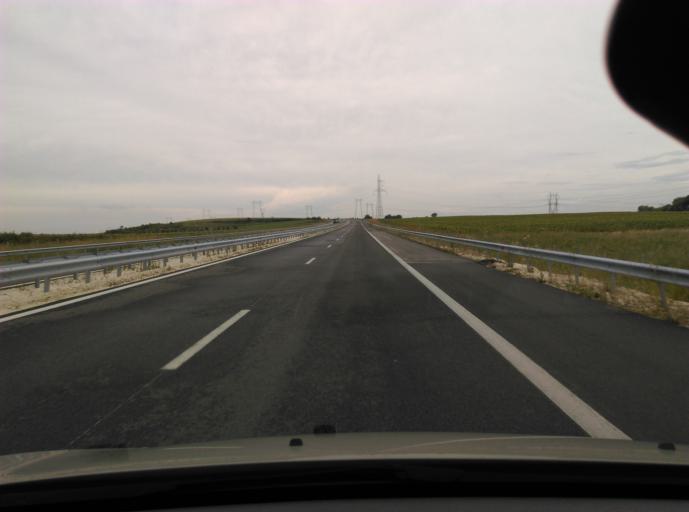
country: BG
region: Stara Zagora
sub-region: Obshtina Chirpan
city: Chirpan
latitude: 42.1249
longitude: 25.3714
